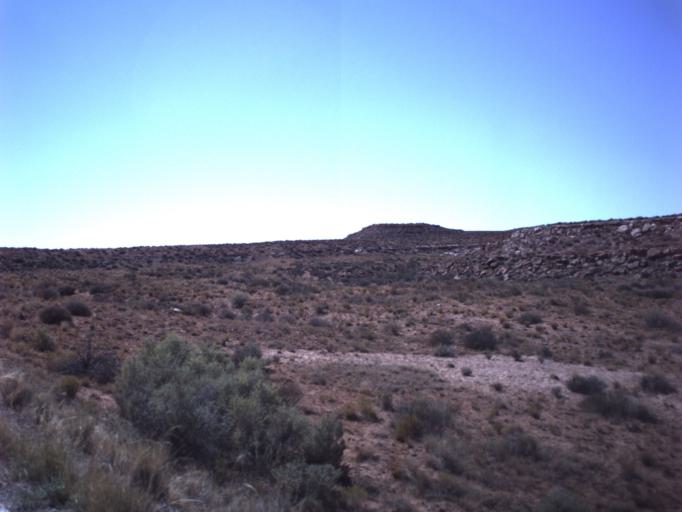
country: US
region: Arizona
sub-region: Navajo County
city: Kayenta
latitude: 37.1917
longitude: -109.9112
